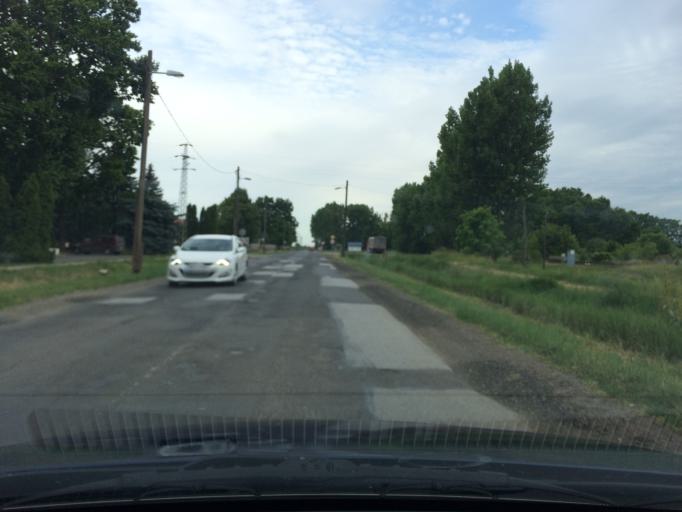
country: HU
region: Hajdu-Bihar
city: Hajdunanas
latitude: 47.9073
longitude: 21.4029
